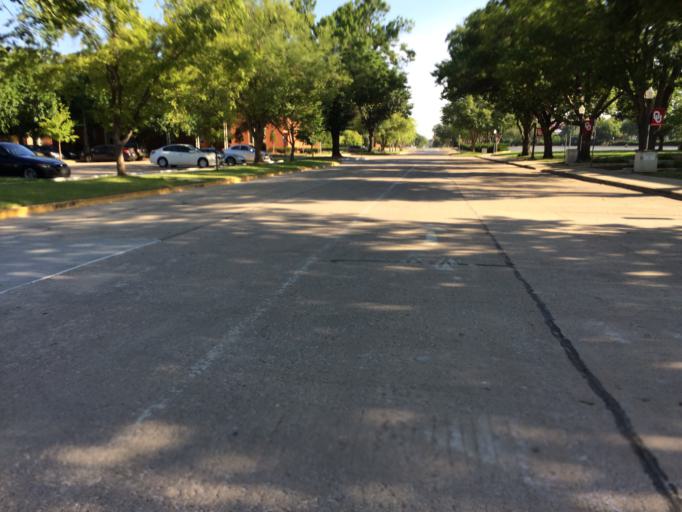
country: US
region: Oklahoma
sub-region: Cleveland County
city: Norman
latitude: 35.1973
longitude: -97.4442
